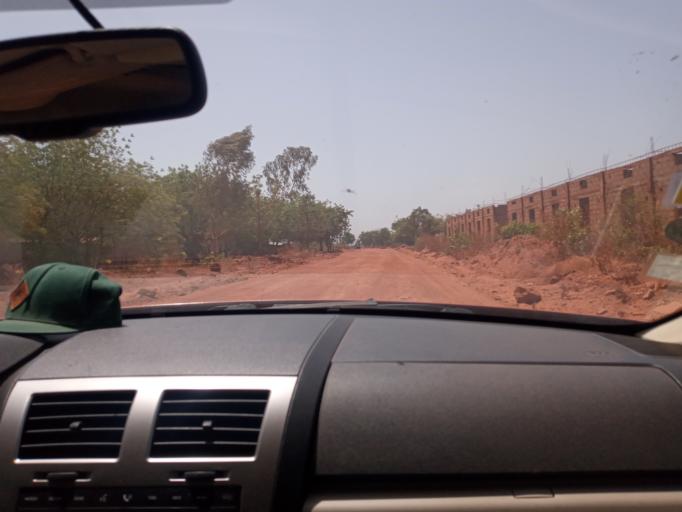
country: ML
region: Bamako
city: Bamako
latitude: 12.5561
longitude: -7.8317
